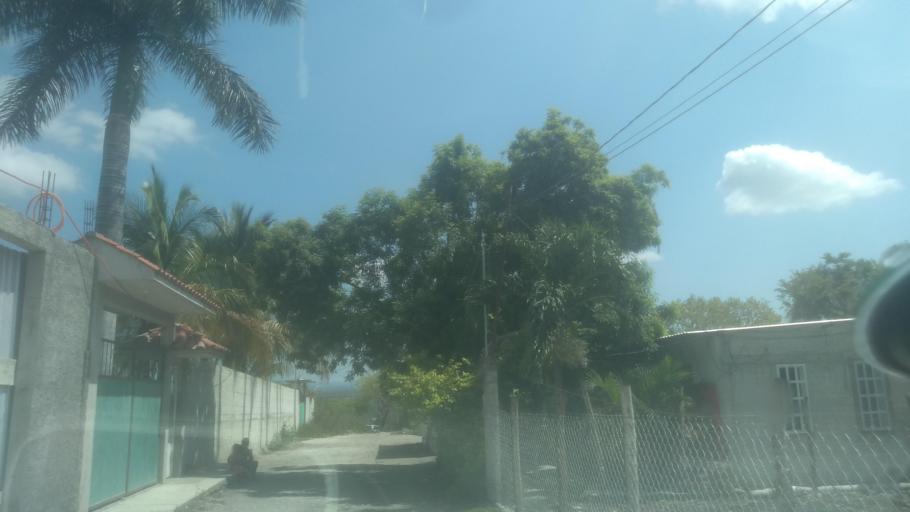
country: MX
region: Veracruz
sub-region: Emiliano Zapata
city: Plan del Rio
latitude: 19.3935
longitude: -96.6348
